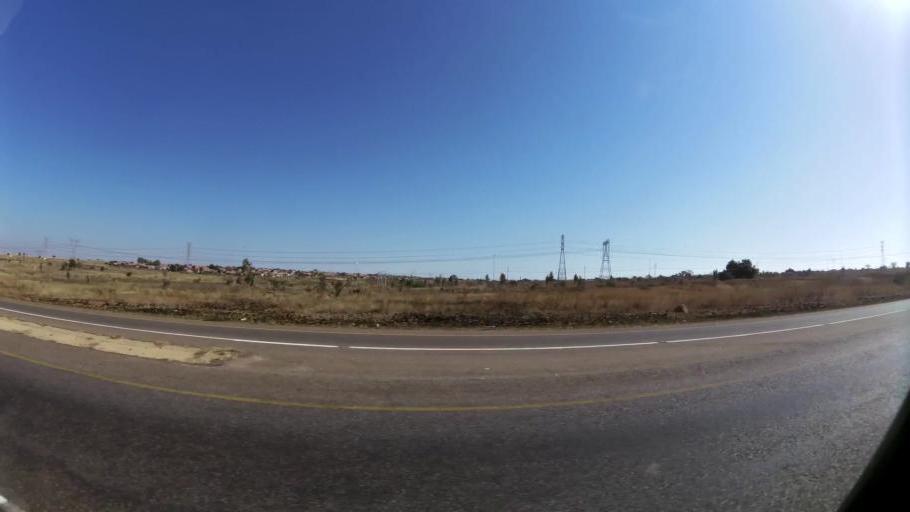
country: ZA
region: Gauteng
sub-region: City of Tshwane Metropolitan Municipality
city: Mabopane
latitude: -25.5528
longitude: 28.1088
